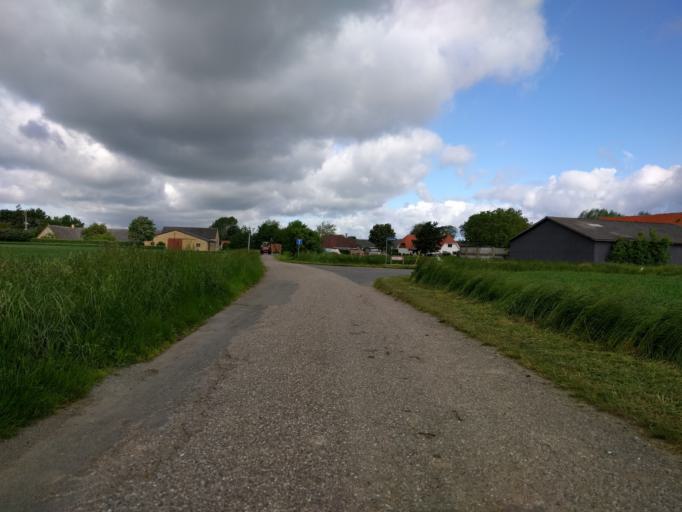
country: DK
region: South Denmark
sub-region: Kerteminde Kommune
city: Kerteminde
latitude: 55.4147
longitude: 10.6245
